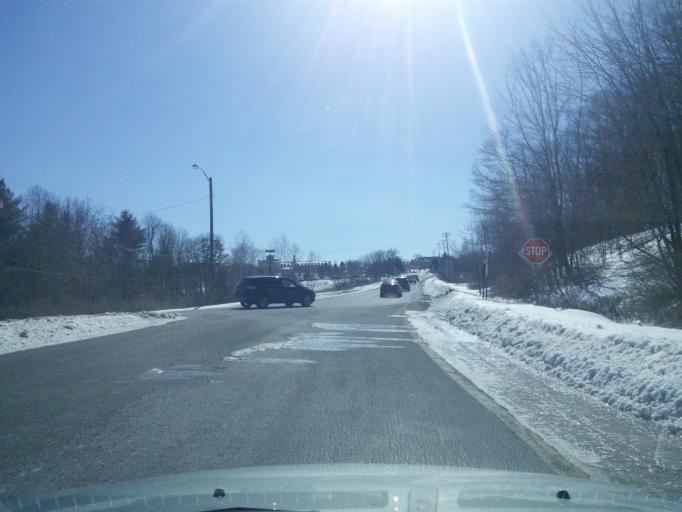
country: US
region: Pennsylvania
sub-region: Centre County
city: Park Forest Village
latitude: 40.8218
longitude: -77.9020
